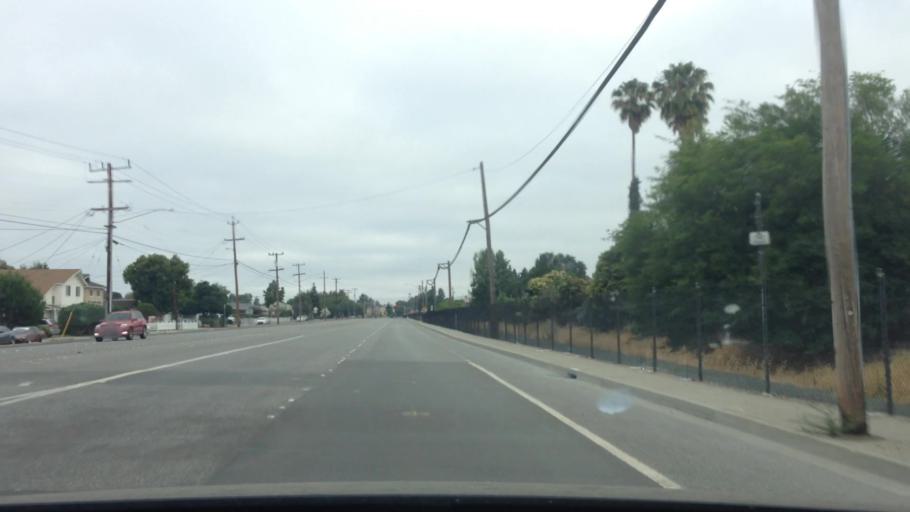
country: US
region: California
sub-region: Alameda County
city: Fremont
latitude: 37.5151
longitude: -121.9528
